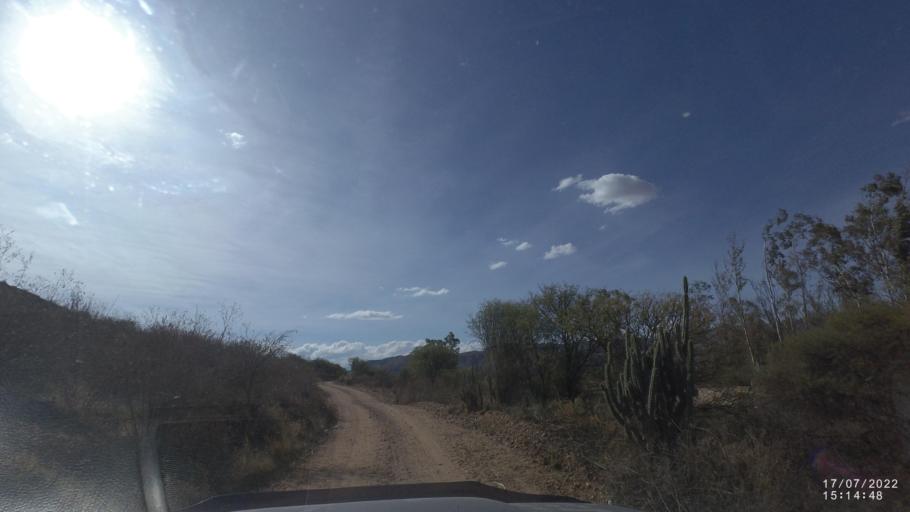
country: BO
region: Cochabamba
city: Capinota
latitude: -17.5604
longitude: -66.2615
